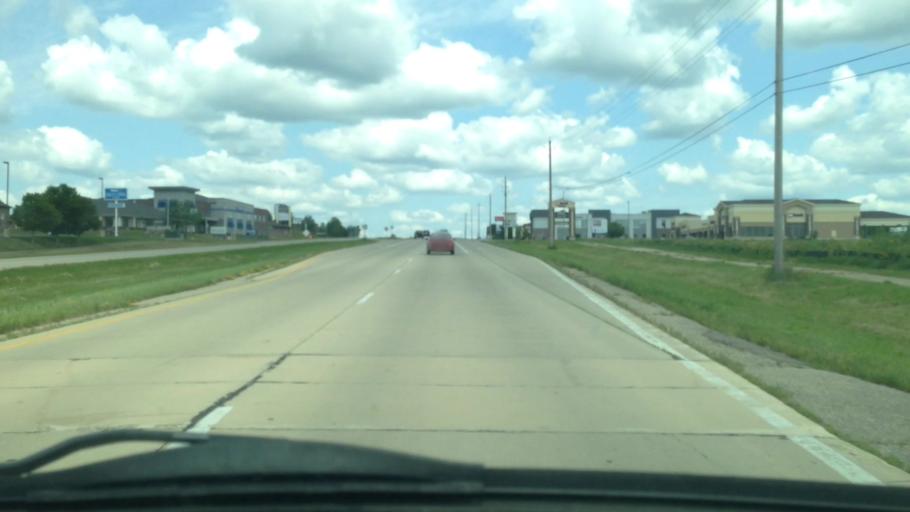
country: US
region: Minnesota
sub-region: Olmsted County
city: Rochester
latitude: 44.0492
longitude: -92.5215
